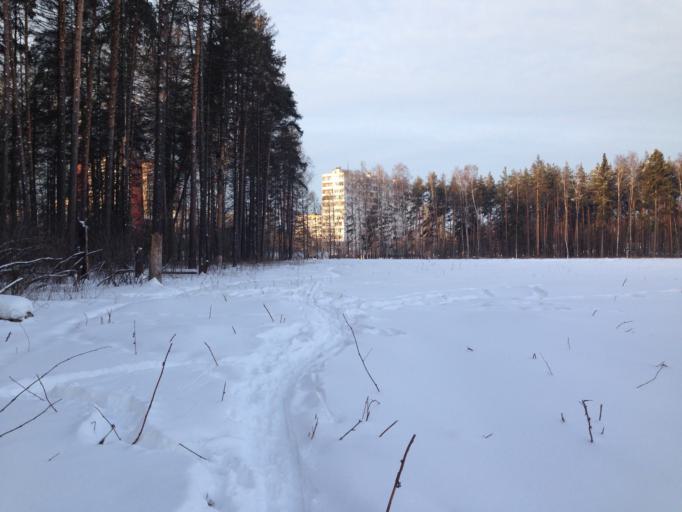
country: RU
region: Moskovskaya
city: Balashikha
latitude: 55.8159
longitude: 37.9736
